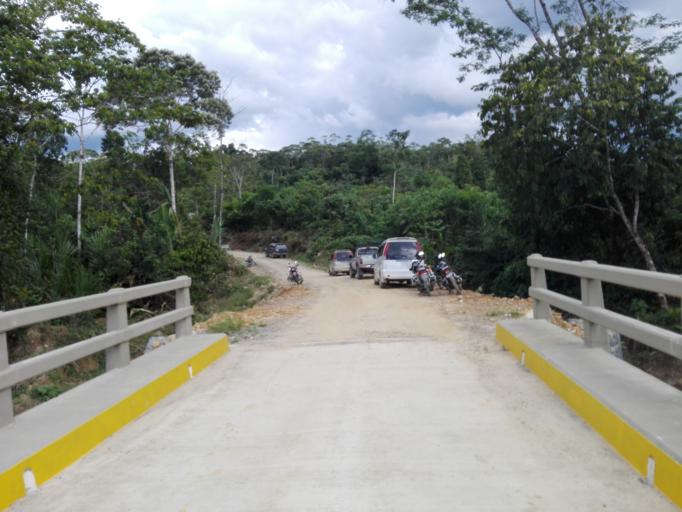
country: BO
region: Cochabamba
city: Chimore
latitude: -17.0473
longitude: -65.0979
